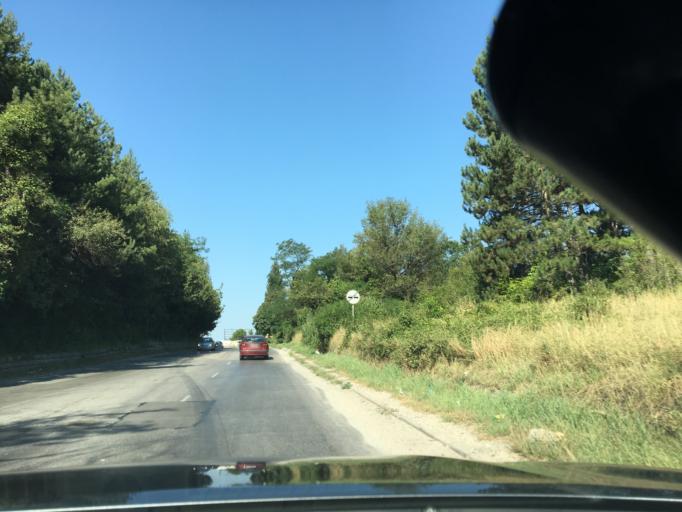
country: BG
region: Sofiya
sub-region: Obshtina Bozhurishte
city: Bozhurishte
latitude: 42.6229
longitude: 23.1852
